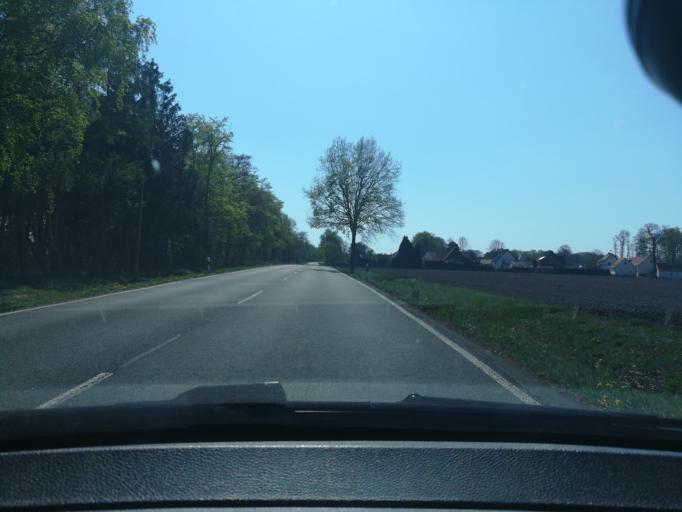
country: DE
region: North Rhine-Westphalia
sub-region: Regierungsbezirk Detmold
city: Harsewinkel
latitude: 52.0151
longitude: 8.2309
